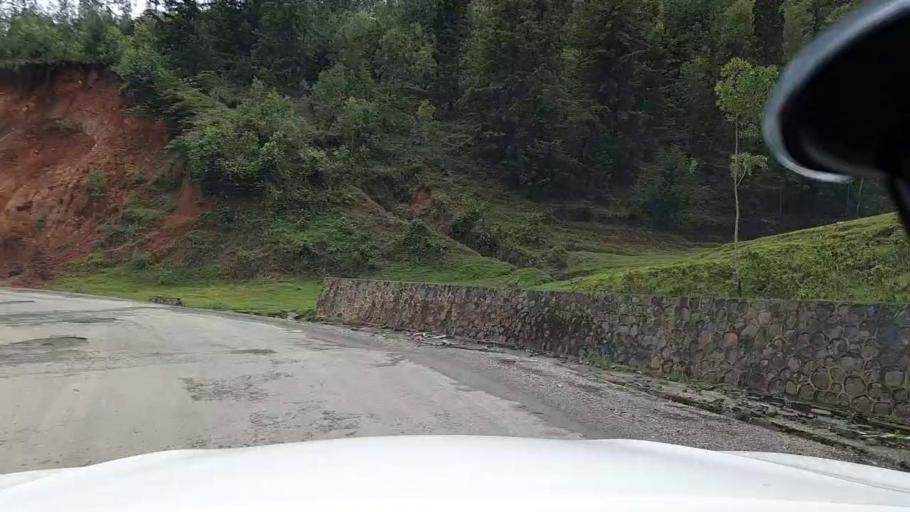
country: RW
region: Southern Province
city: Gitarama
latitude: -2.0613
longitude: 29.5607
